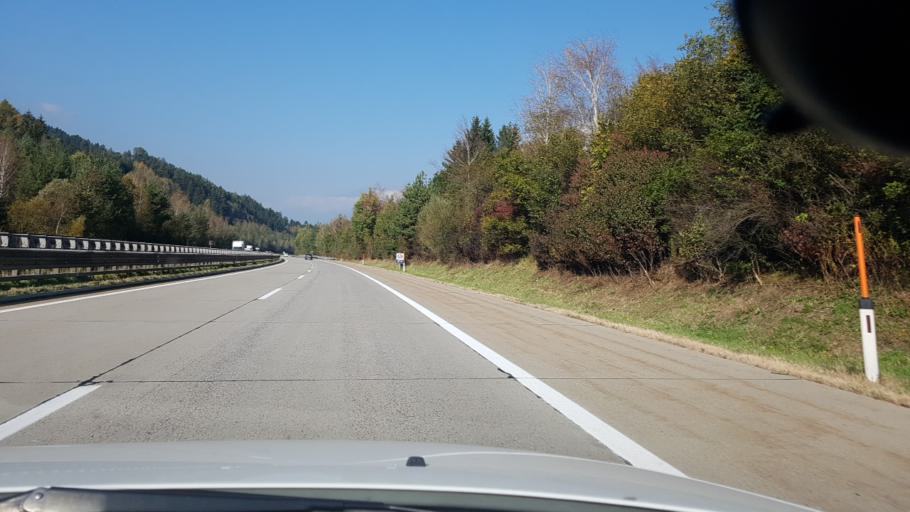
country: AT
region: Carinthia
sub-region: Politischer Bezirk Villach Land
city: Ferndorf
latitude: 46.7424
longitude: 13.5852
